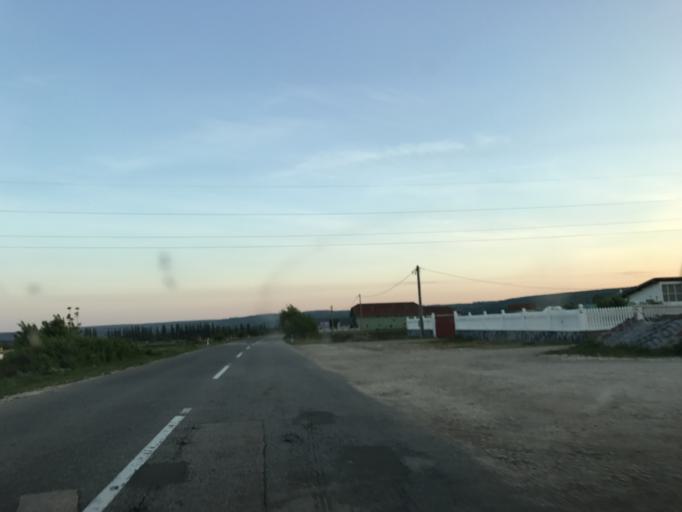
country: RS
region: Central Serbia
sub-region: Borski Okrug
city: Negotin
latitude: 44.2516
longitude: 22.5195
